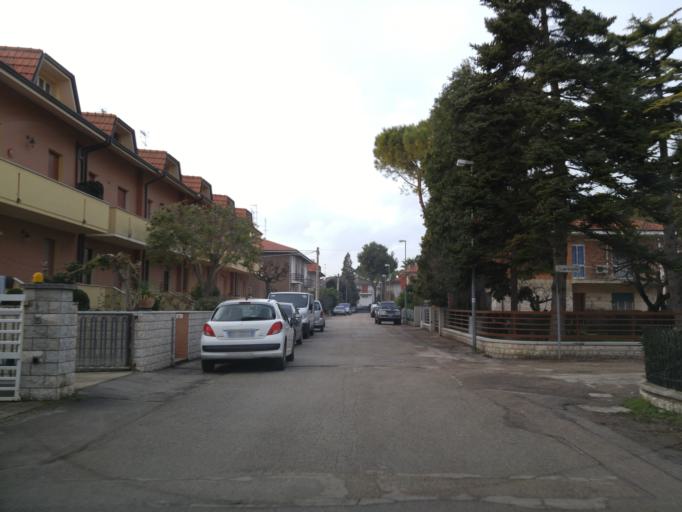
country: IT
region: The Marches
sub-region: Provincia di Pesaro e Urbino
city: Centinarola
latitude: 43.8296
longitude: 13.0022
